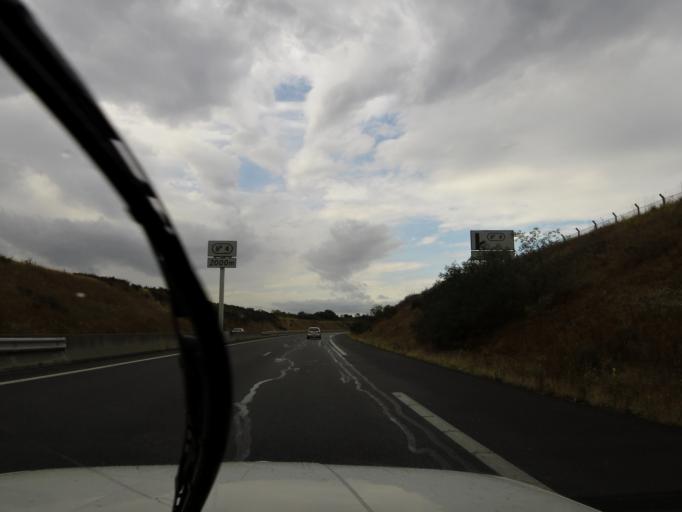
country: FR
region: Rhone-Alpes
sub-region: Departement de l'Isere
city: Satolas-et-Bonce
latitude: 45.7083
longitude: 5.0994
